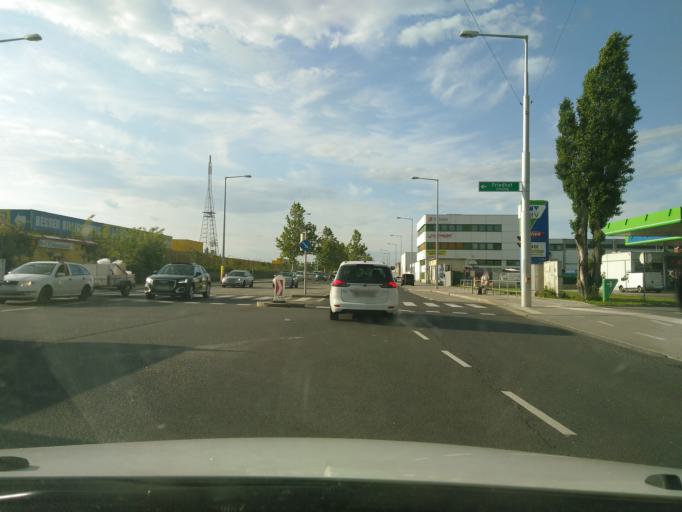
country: AT
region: Lower Austria
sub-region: Politischer Bezirk Modling
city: Brunn am Gebirge
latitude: 48.1330
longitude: 16.2980
